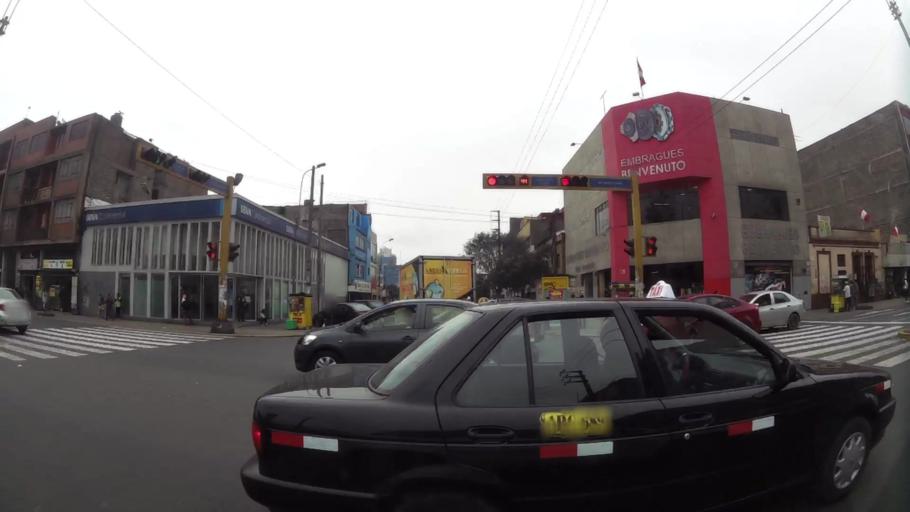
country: PE
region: Lima
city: Lima
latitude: -12.0618
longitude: -77.0294
